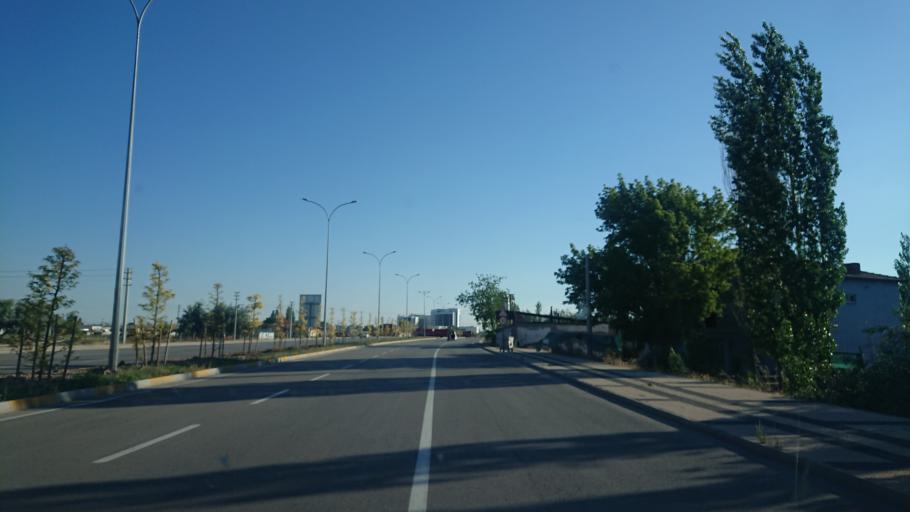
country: TR
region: Aksaray
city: Aksaray
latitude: 38.3811
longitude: 33.9909
